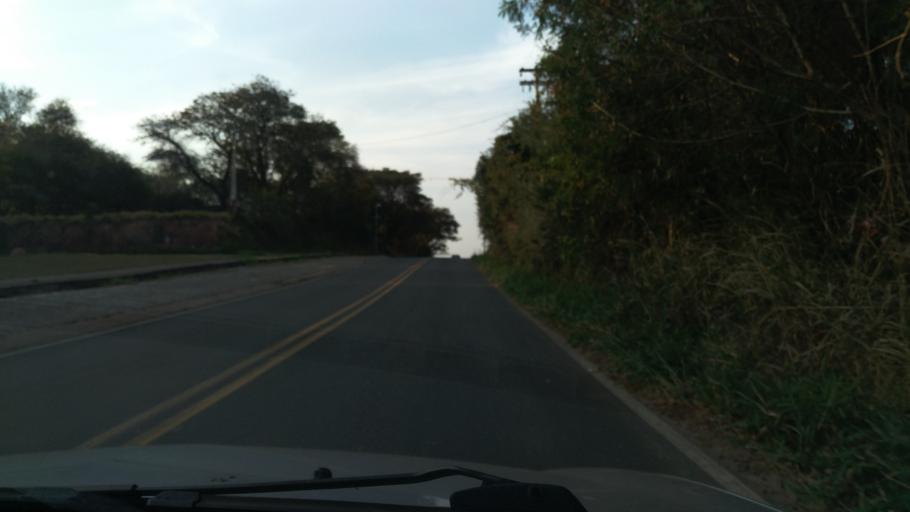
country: BR
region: Sao Paulo
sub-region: Vinhedo
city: Vinhedo
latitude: -23.0074
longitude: -47.0020
